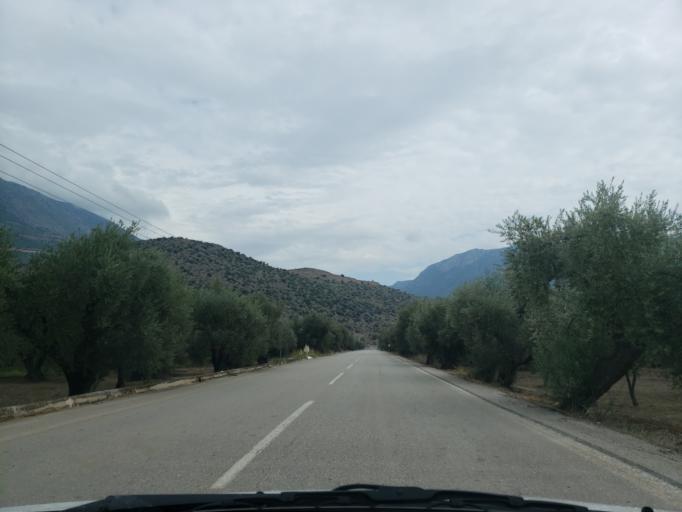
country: GR
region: Central Greece
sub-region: Nomos Fokidos
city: Kirra
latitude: 38.4784
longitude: 22.4471
